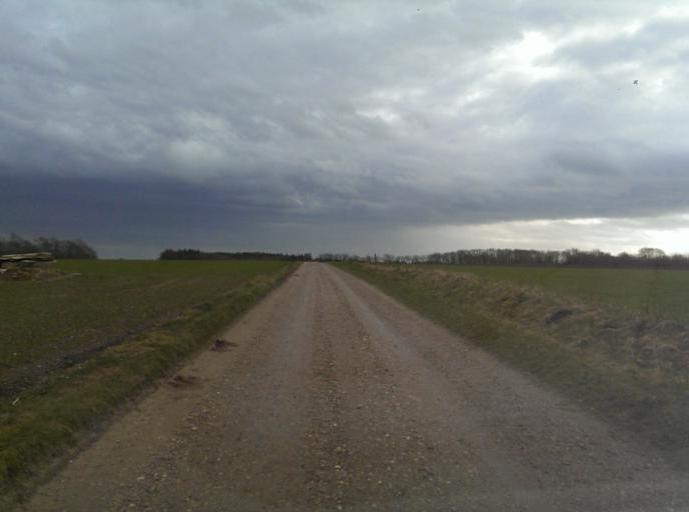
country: DK
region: South Denmark
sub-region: Esbjerg Kommune
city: Tjaereborg
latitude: 55.4875
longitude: 8.5978
